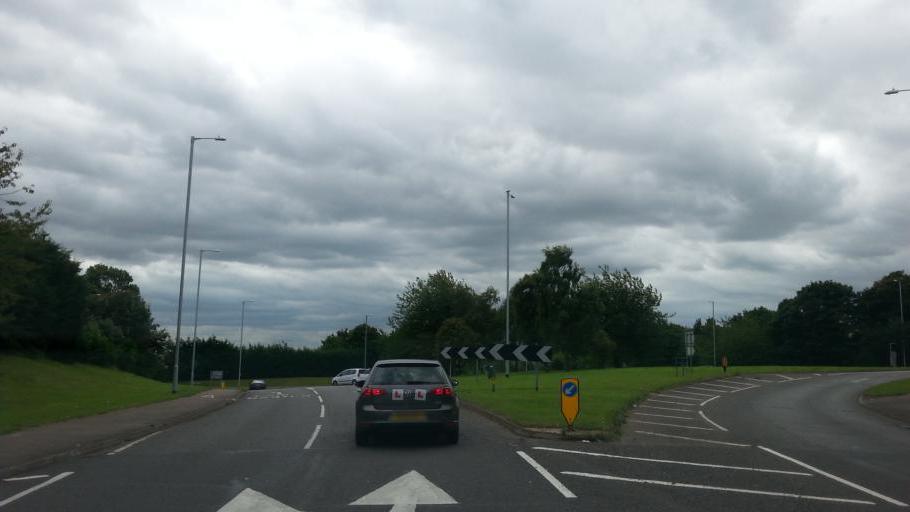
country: GB
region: England
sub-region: Northamptonshire
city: Earls Barton
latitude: 52.2626
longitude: -0.8107
